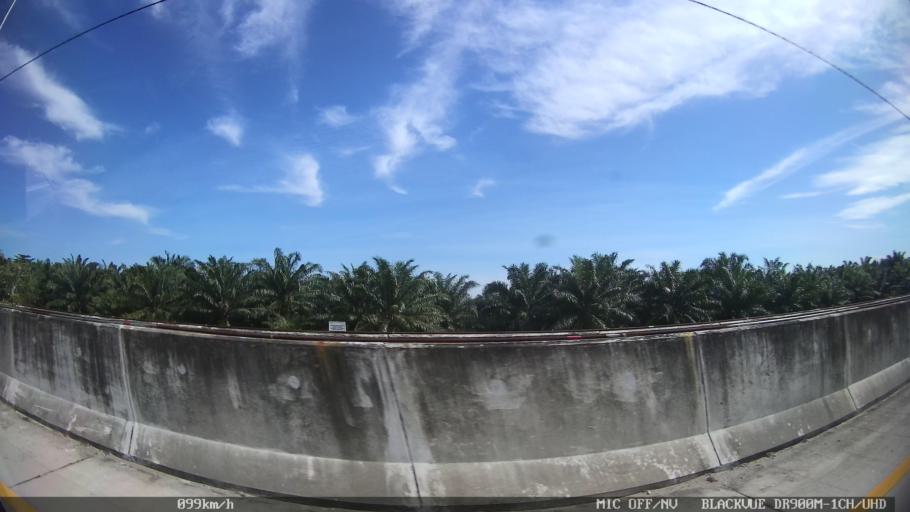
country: ID
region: North Sumatra
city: Sunggal
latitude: 3.6385
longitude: 98.6145
